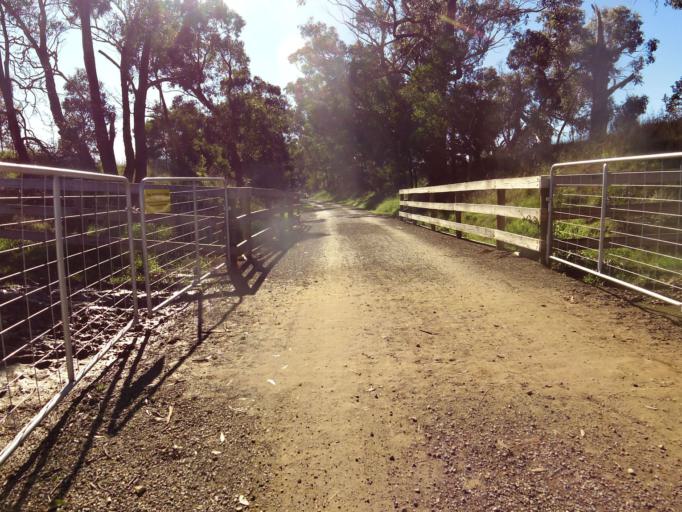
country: AU
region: Victoria
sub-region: Yarra Ranges
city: Lilydale
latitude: -37.7309
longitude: 145.3717
